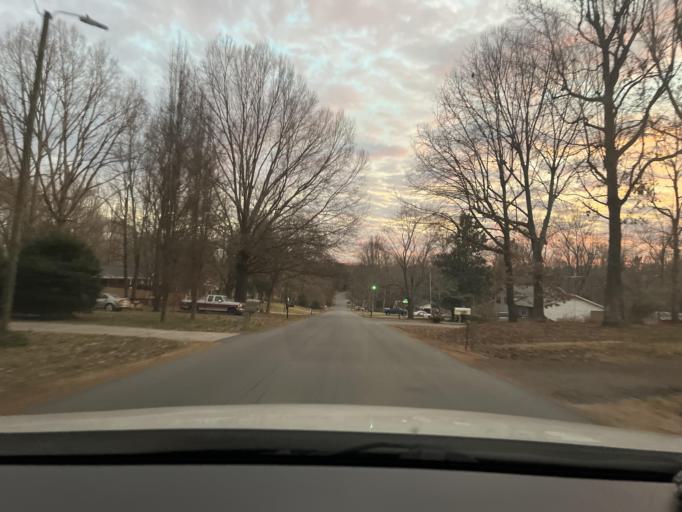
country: US
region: North Carolina
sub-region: Guilford County
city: Pleasant Garden
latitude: 36.0092
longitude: -79.7622
